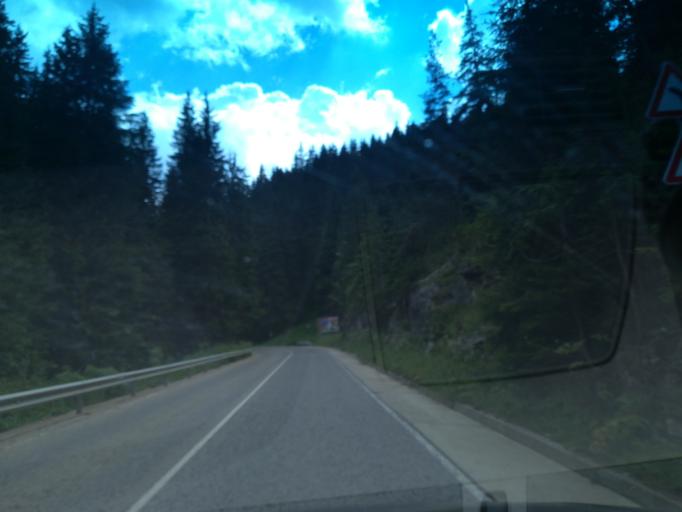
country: BG
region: Smolyan
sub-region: Obshtina Chepelare
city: Chepelare
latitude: 41.6634
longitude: 24.7139
